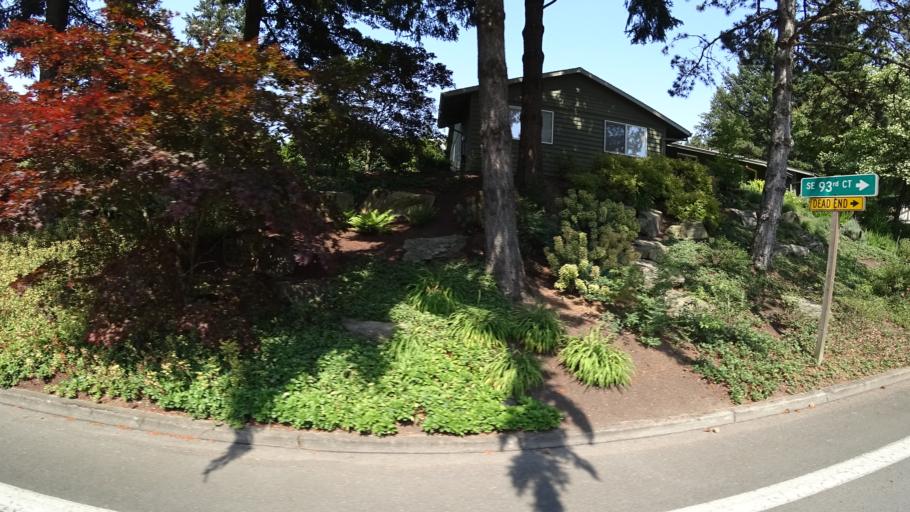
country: US
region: Oregon
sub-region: Multnomah County
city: Lents
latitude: 45.4463
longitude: -122.5667
